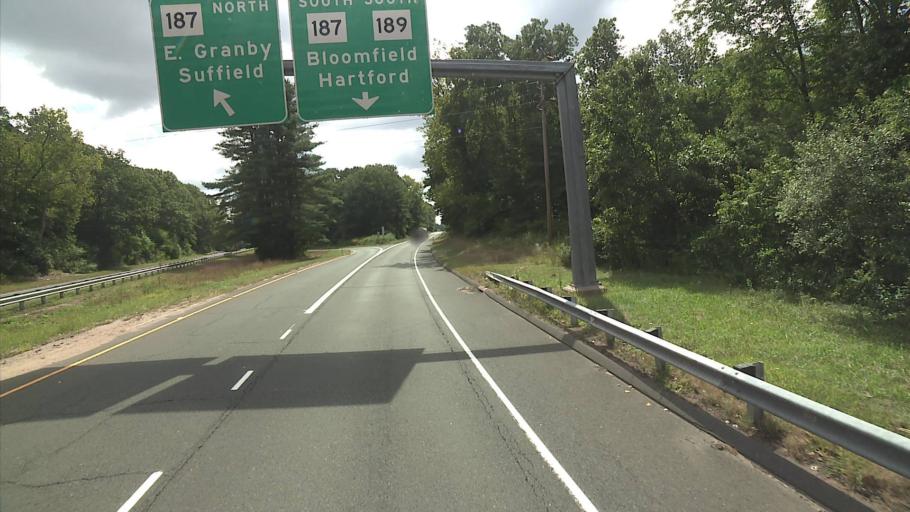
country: US
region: Connecticut
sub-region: Hartford County
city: Tariffville
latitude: 41.8977
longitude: -72.7536
